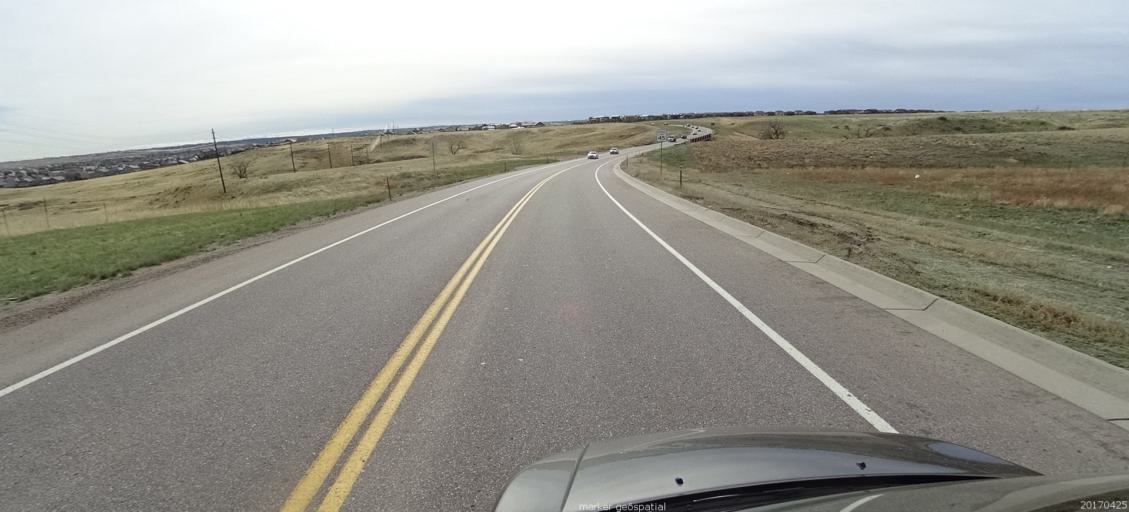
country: US
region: Colorado
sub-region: Douglas County
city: Stonegate
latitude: 39.5214
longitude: -104.8380
